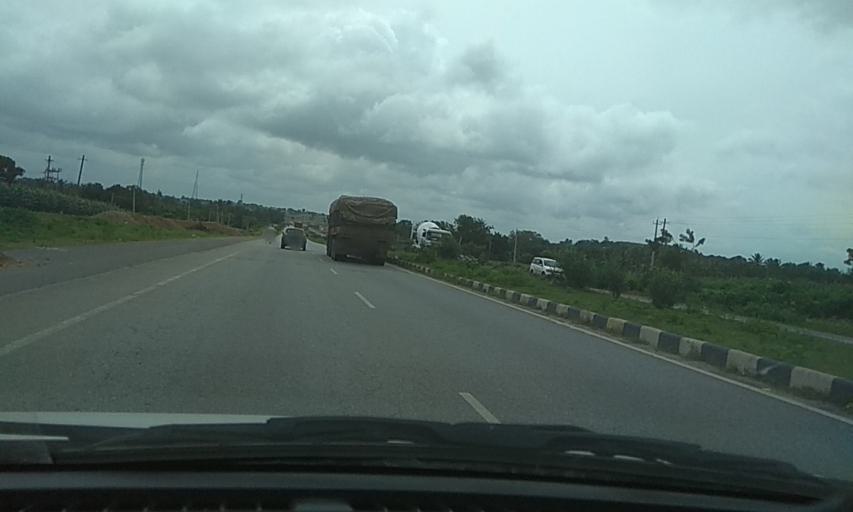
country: IN
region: Karnataka
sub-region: Davanagere
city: Mayakonda
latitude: 14.3668
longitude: 76.1522
